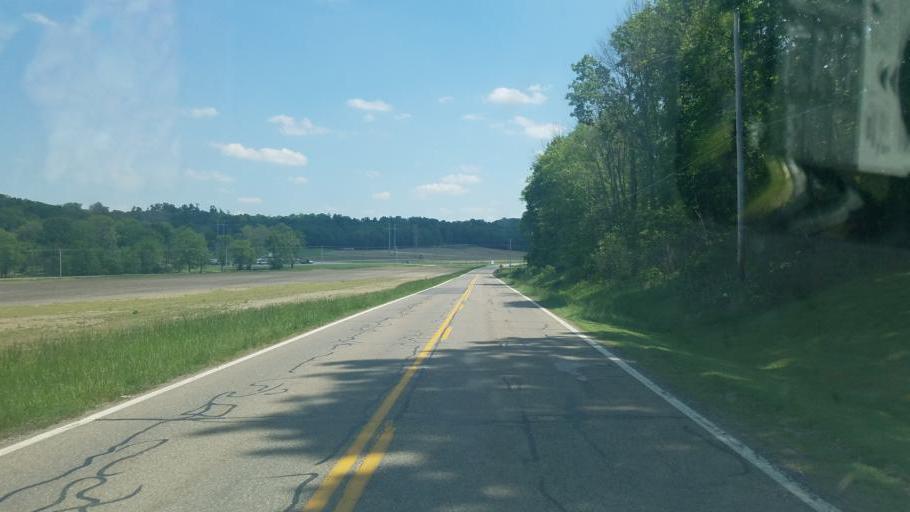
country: US
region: Ohio
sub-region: Muskingum County
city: Frazeysburg
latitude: 40.0844
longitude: -82.1614
